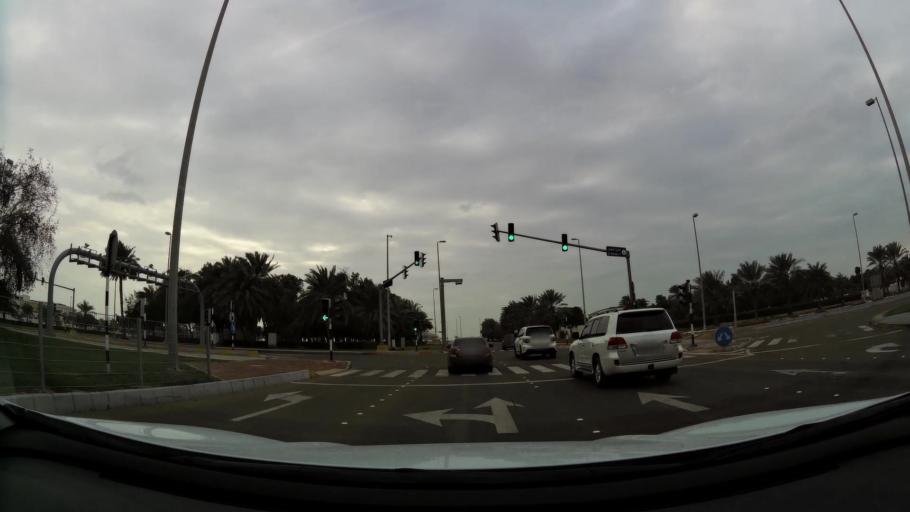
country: AE
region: Abu Dhabi
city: Abu Dhabi
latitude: 24.4324
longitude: 54.3734
